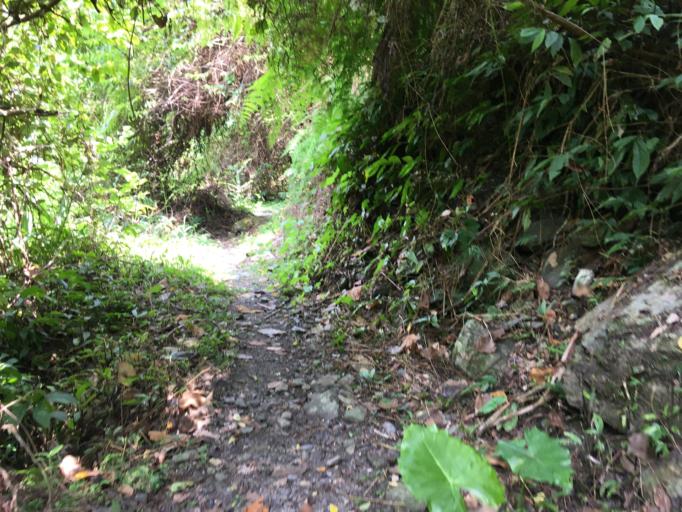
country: TW
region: Taiwan
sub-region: Yilan
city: Yilan
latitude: 24.4220
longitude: 121.6968
